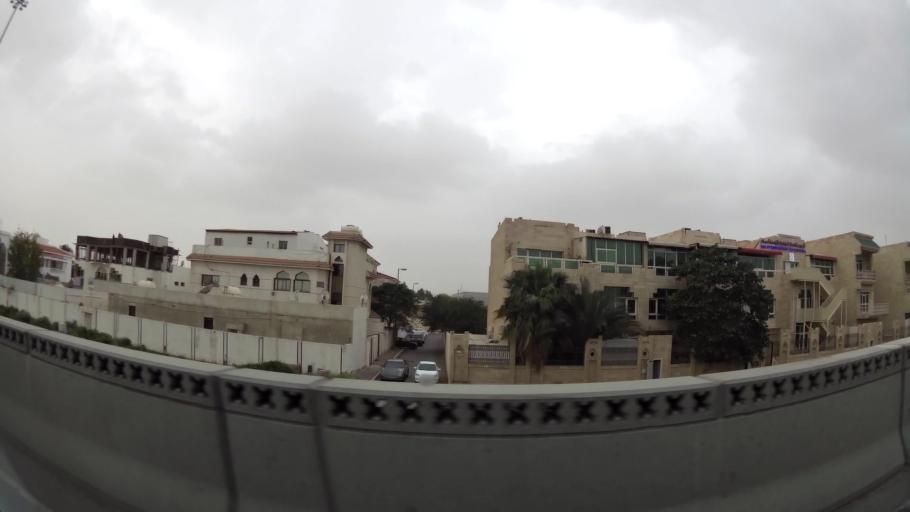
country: AE
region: Abu Dhabi
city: Abu Dhabi
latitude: 24.4531
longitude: 54.4047
